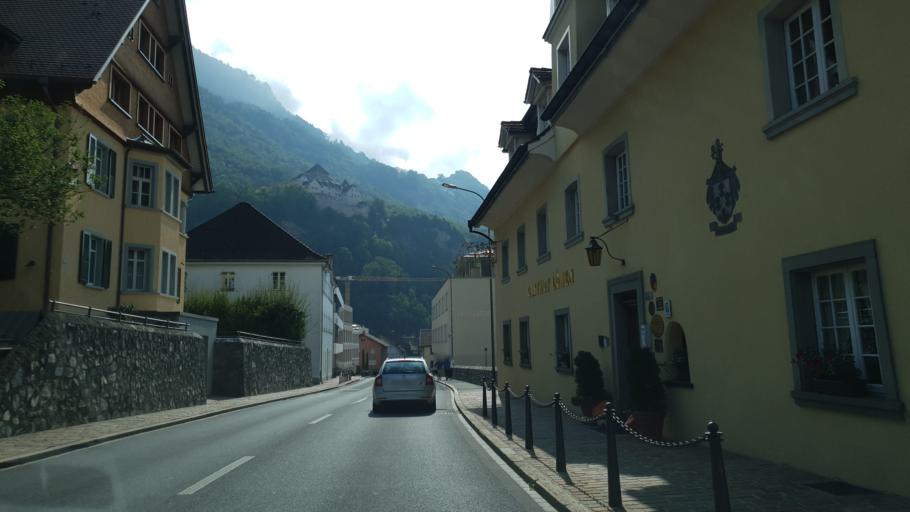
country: LI
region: Vaduz
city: Vaduz
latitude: 47.1429
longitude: 9.5186
